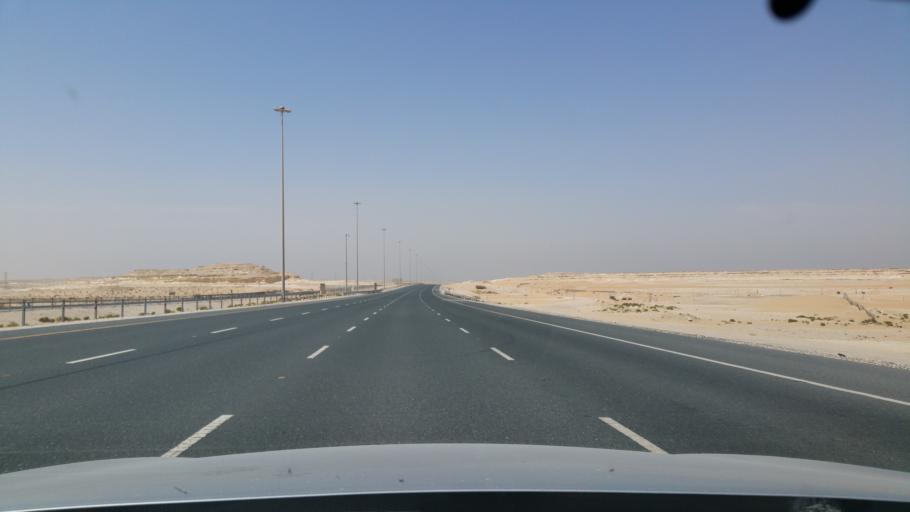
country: QA
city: Umm Bab
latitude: 24.8646
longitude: 50.9063
